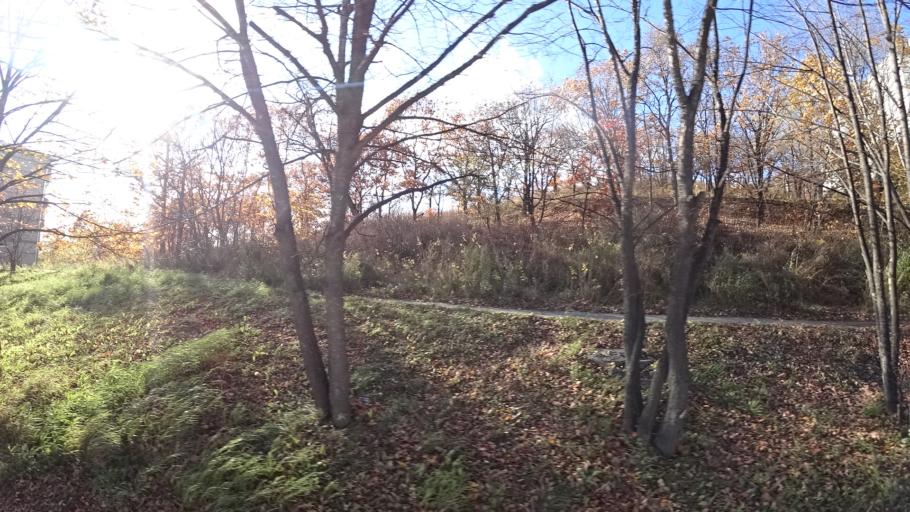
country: RU
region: Khabarovsk Krai
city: Amursk
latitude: 50.2409
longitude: 136.9050
